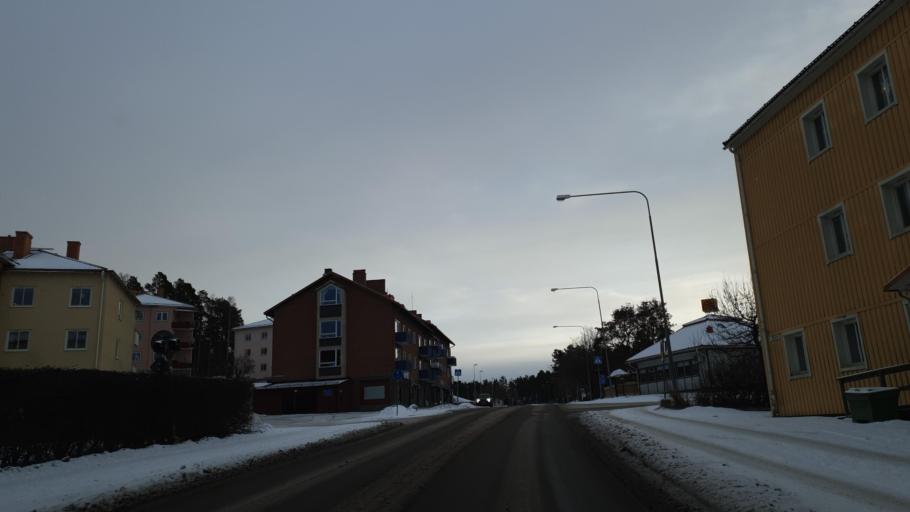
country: SE
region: Gaevleborg
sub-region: Soderhamns Kommun
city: Soderhamn
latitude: 61.2989
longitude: 17.0571
